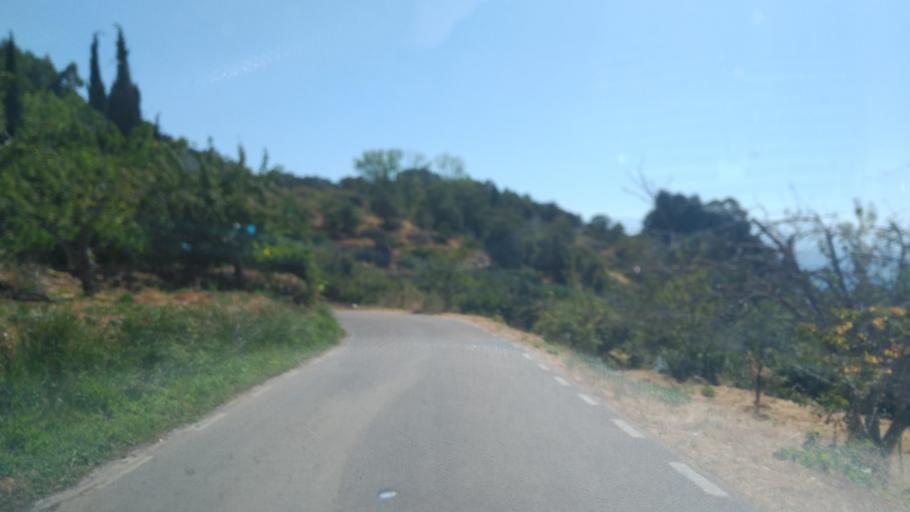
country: ES
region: Castille and Leon
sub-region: Provincia de Salamanca
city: San Martin del Castanar
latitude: 40.5262
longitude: -6.0676
